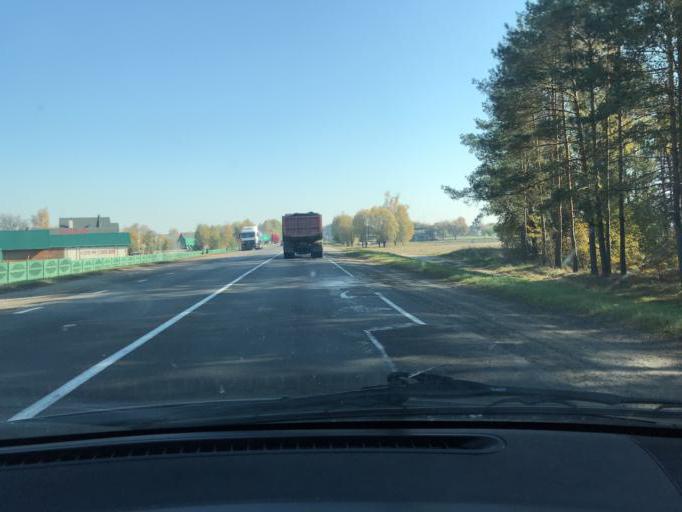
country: BY
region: Brest
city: Luninyets
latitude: 52.2745
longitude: 26.9226
